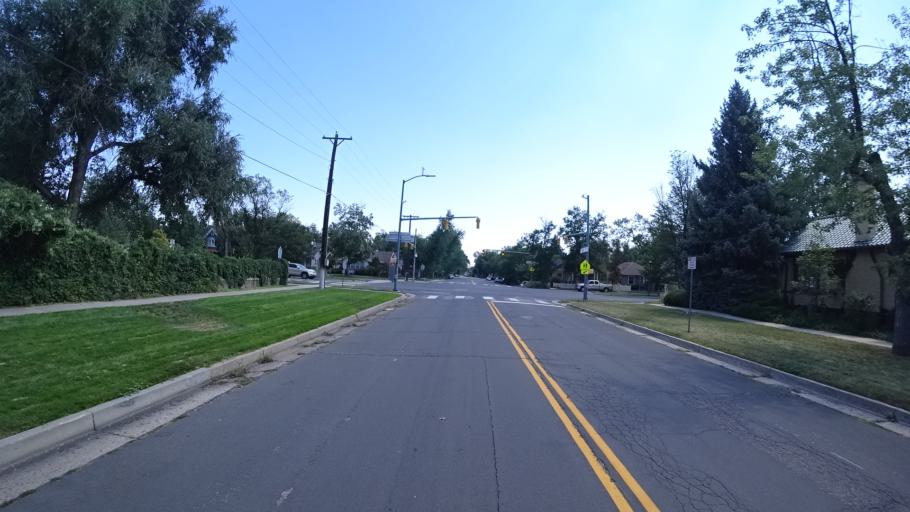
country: US
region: Colorado
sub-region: El Paso County
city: Colorado Springs
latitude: 38.8579
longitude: -104.8246
